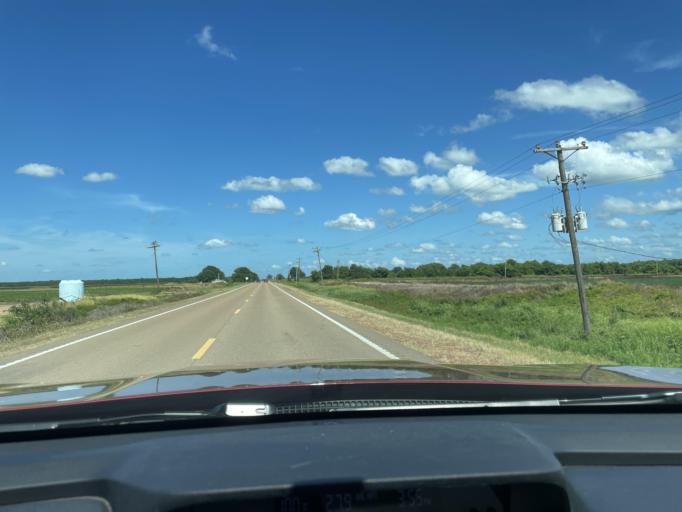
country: US
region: Mississippi
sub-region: Humphreys County
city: Belzoni
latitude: 33.1829
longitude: -90.6499
